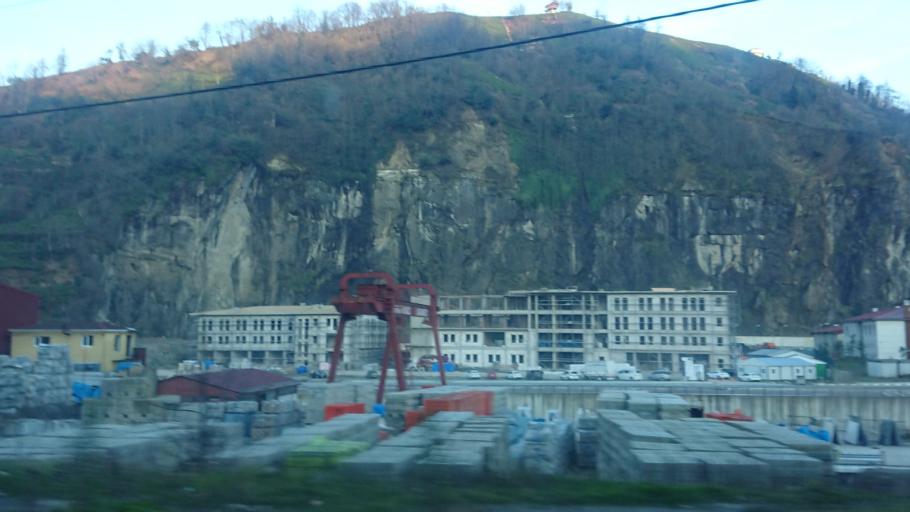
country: TR
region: Rize
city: Gundogdu
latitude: 41.0290
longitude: 40.5816
